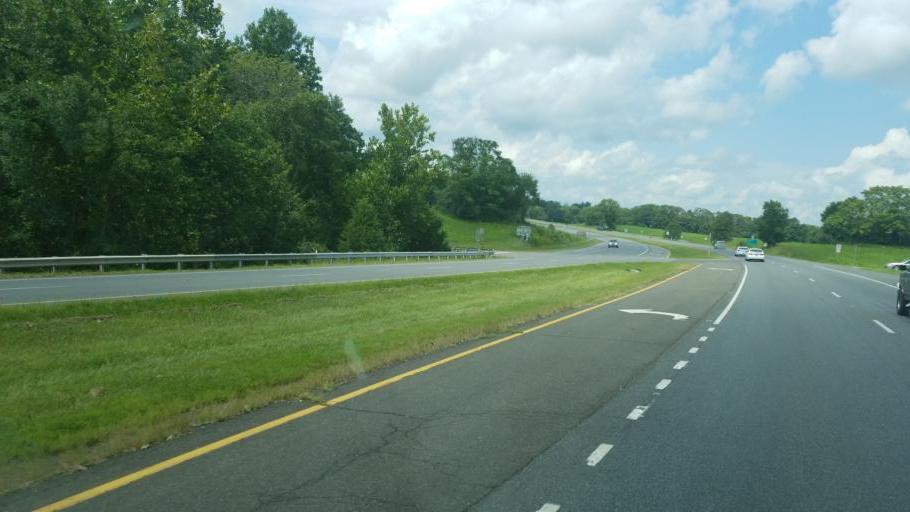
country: US
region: Virginia
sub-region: Fauquier County
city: Marshall
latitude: 38.8284
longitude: -77.8161
